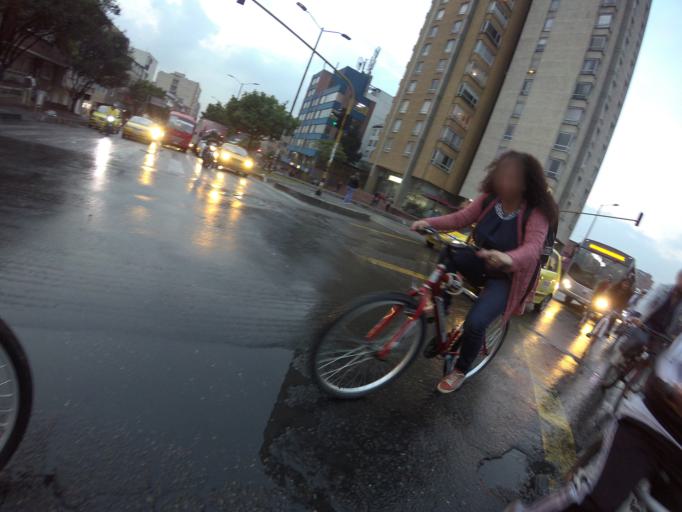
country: CO
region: Bogota D.C.
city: Bogota
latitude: 4.6395
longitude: -74.0630
